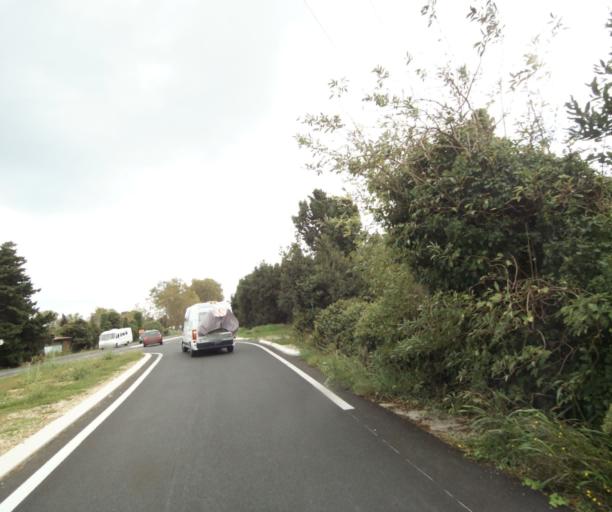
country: FR
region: Languedoc-Roussillon
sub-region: Departement des Pyrenees-Orientales
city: Elne
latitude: 42.5929
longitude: 2.9781
